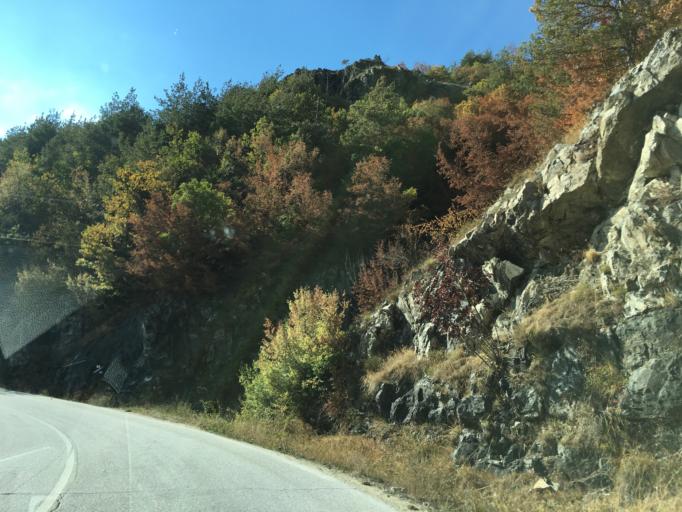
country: BG
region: Smolyan
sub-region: Obshtina Madan
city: Madan
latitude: 41.4527
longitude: 24.9871
